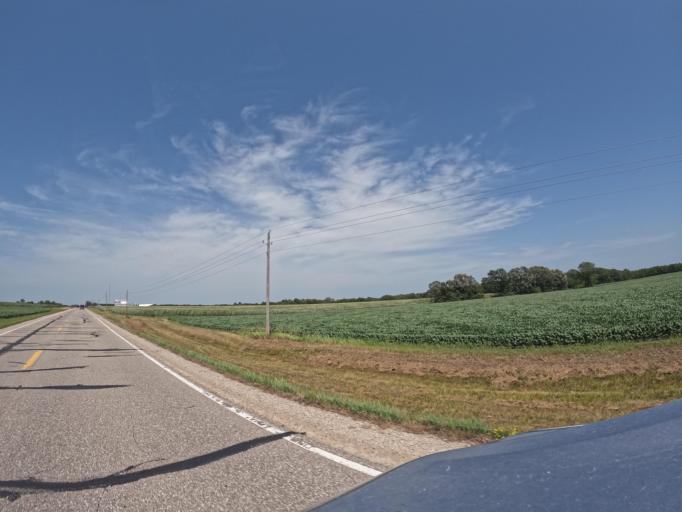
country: US
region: Iowa
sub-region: Henry County
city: Mount Pleasant
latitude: 40.9948
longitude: -91.6122
